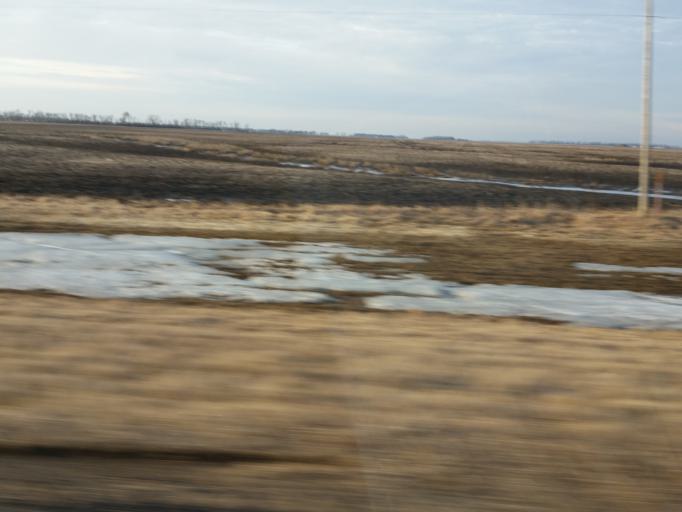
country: US
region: North Dakota
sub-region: Traill County
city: Mayville
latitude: 47.3531
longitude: -97.2378
